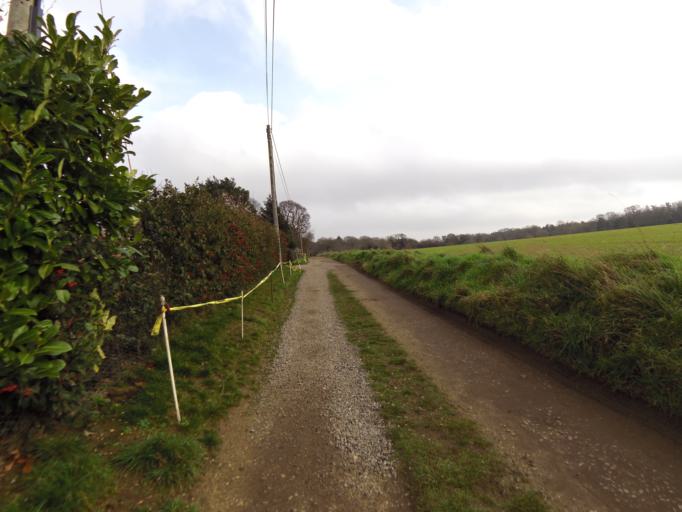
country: GB
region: England
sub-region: Suffolk
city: Woodbridge
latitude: 52.0734
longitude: 1.2856
